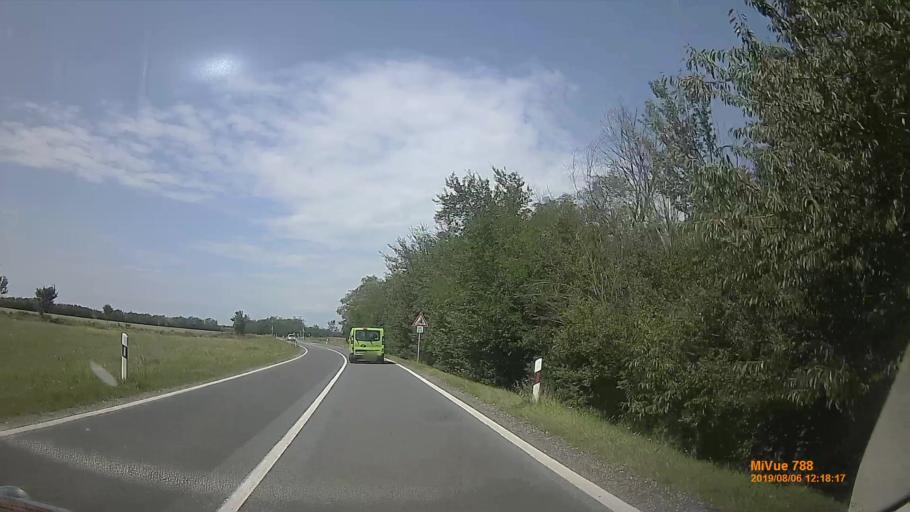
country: HU
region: Vas
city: Vep
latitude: 47.1692
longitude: 16.7785
